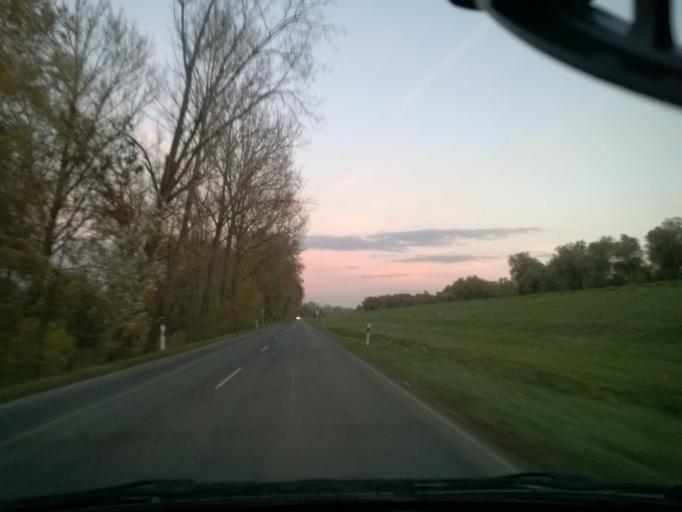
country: HU
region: Csongrad
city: Szentes
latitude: 46.6811
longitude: 20.2164
